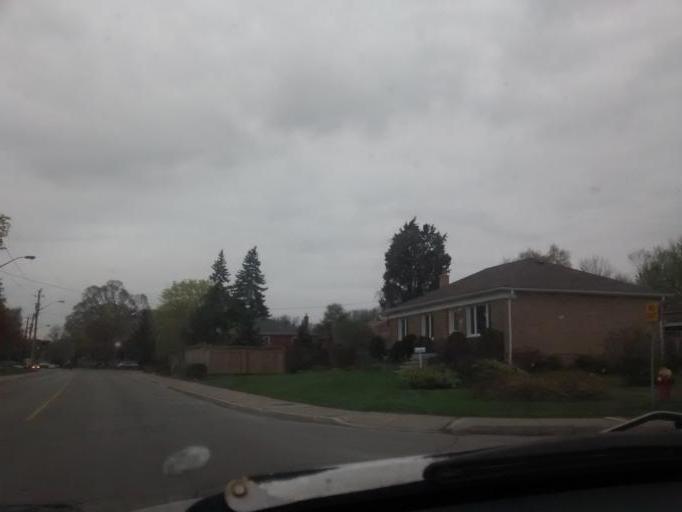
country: CA
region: Ontario
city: Burlington
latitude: 43.3367
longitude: -79.7957
